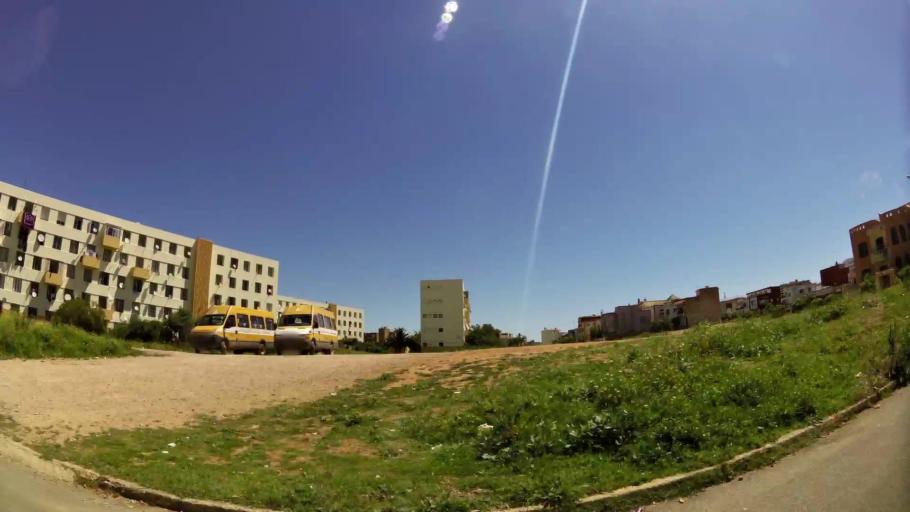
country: MA
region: Meknes-Tafilalet
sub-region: Meknes
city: Meknes
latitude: 33.9013
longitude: -5.5241
